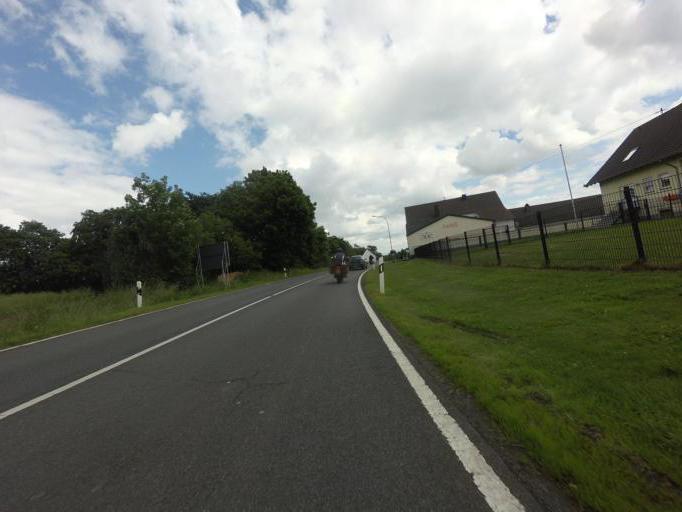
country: DE
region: Rheinland-Pfalz
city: Hirten
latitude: 50.3323
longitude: 7.1056
